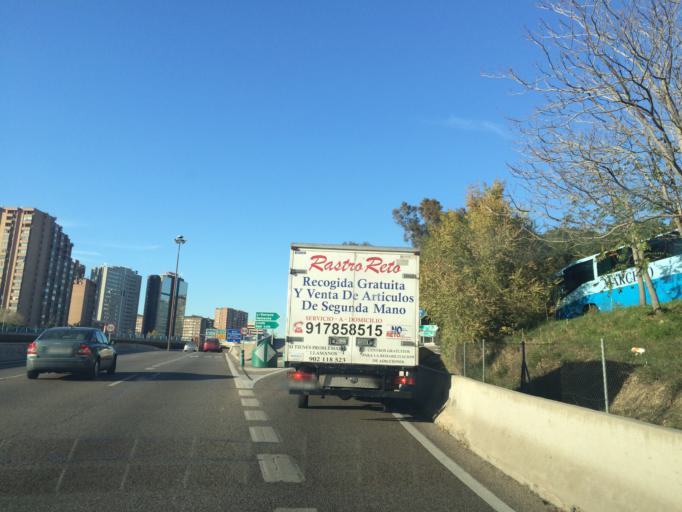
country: ES
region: Madrid
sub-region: Provincia de Madrid
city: Pinar de Chamartin
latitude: 40.4699
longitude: -3.6704
